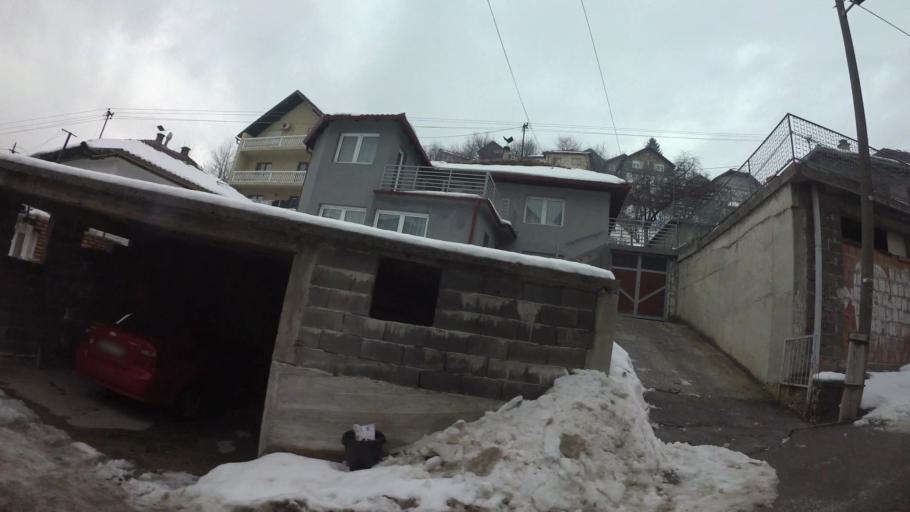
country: BA
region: Federation of Bosnia and Herzegovina
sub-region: Kanton Sarajevo
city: Sarajevo
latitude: 43.8542
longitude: 18.3541
